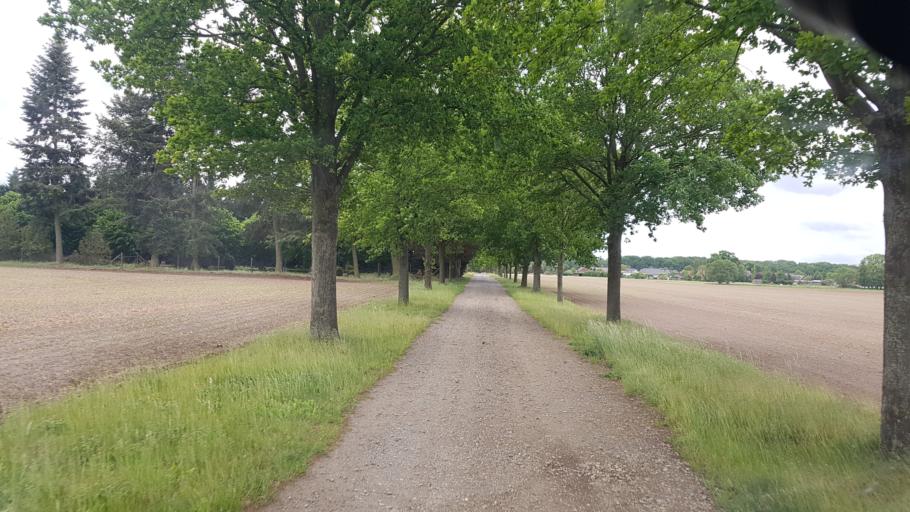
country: DE
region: Brandenburg
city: Schonewalde
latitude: 51.7081
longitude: 13.6024
